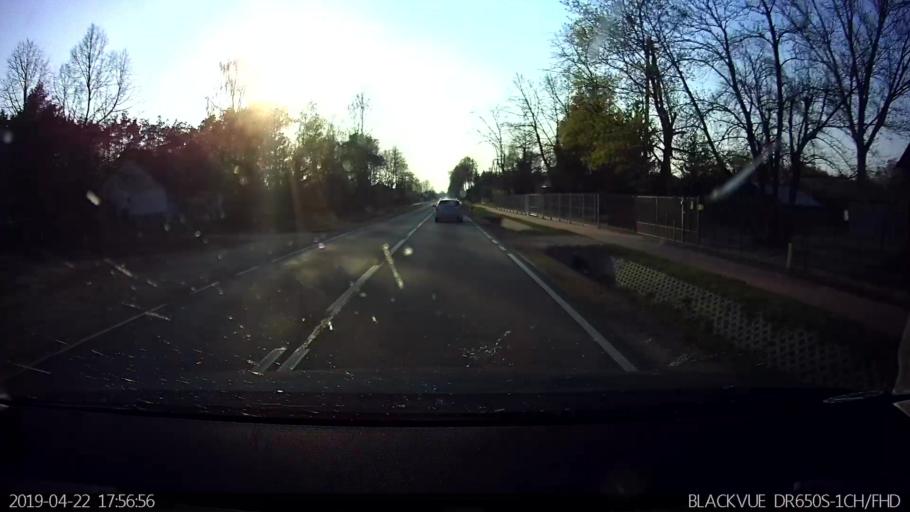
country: PL
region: Masovian Voivodeship
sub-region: Powiat wegrowski
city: Korytnica
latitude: 52.4669
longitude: 21.8997
